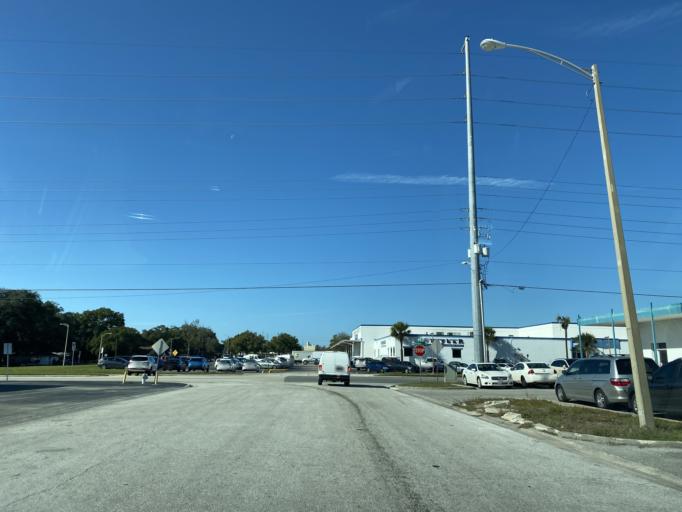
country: US
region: Florida
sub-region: Orange County
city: Holden Heights
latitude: 28.5151
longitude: -81.3841
